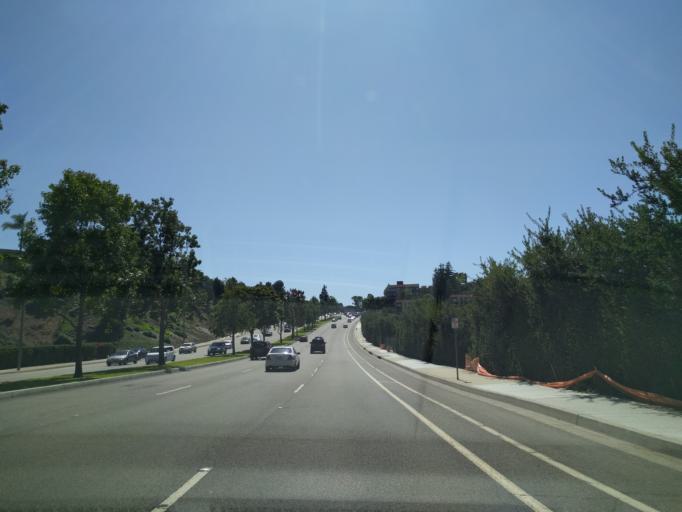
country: US
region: California
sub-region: Orange County
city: San Joaquin Hills
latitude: 33.6291
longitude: -117.8766
